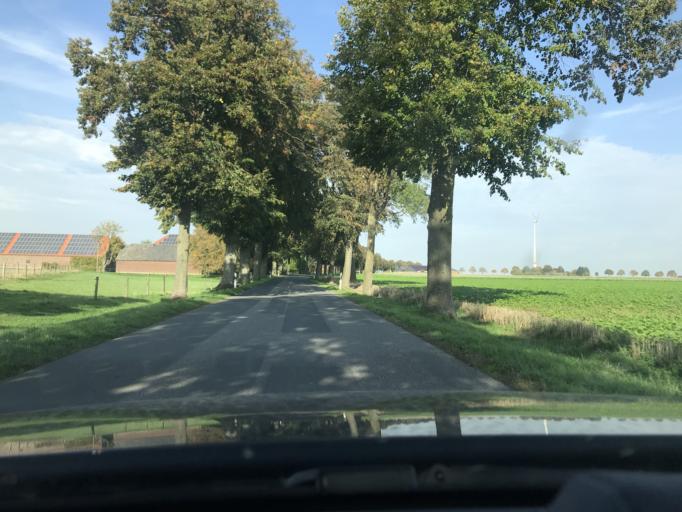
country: DE
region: North Rhine-Westphalia
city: Kalkar
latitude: 51.7091
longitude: 6.2676
